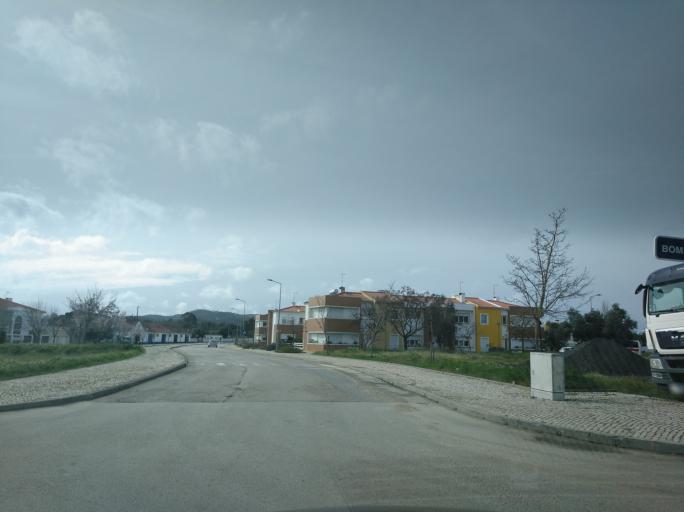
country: PT
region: Setubal
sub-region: Grandola
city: Grandola
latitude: 38.1770
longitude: -8.5714
